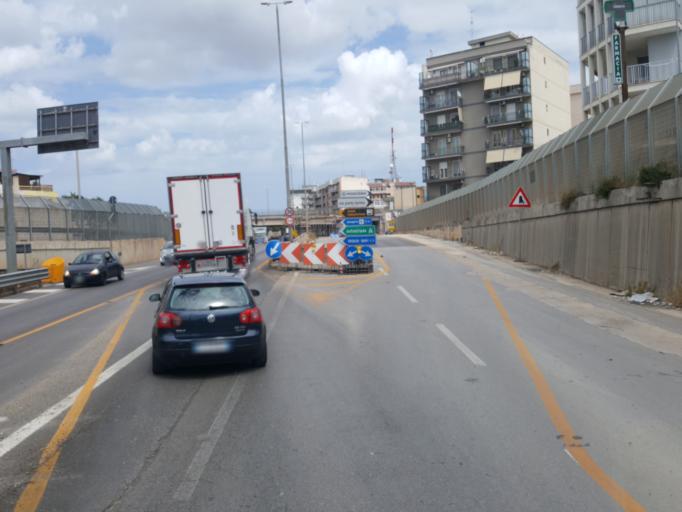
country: IT
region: Apulia
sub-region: Provincia di Bari
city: Modugno
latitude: 41.0882
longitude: 16.7789
